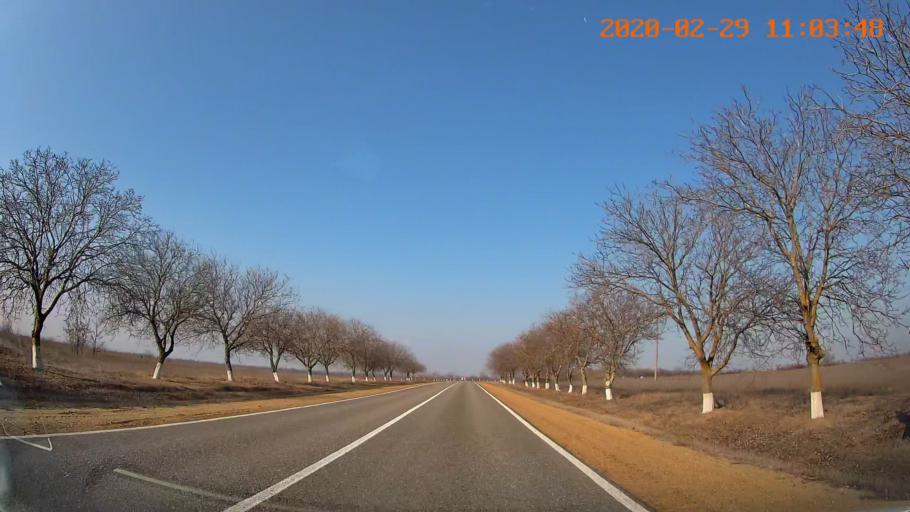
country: MD
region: Criuleni
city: Criuleni
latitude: 47.1819
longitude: 29.2108
